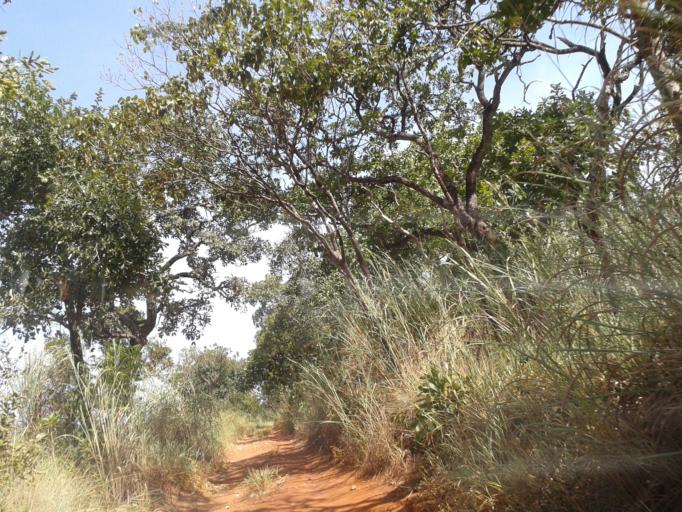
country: BR
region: Minas Gerais
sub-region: Campina Verde
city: Campina Verde
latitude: -19.5053
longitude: -49.5653
